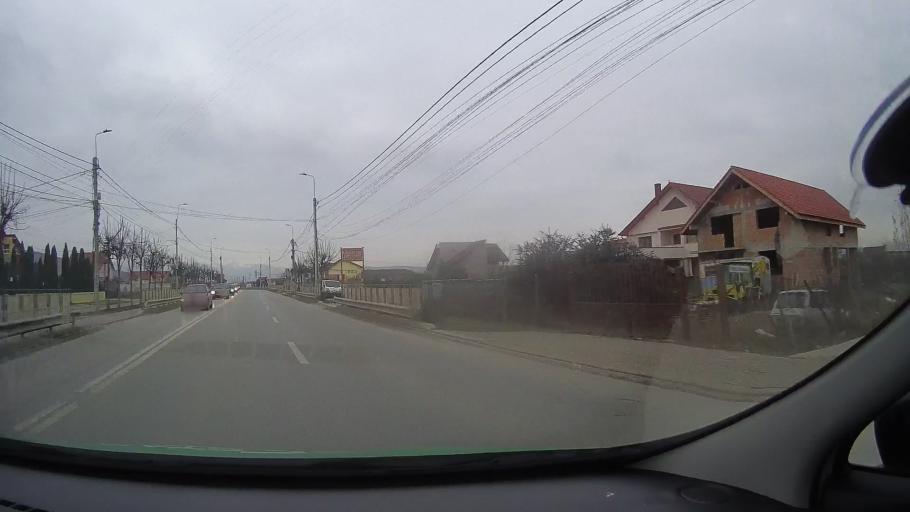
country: RO
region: Alba
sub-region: Municipiul Alba Iulia
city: Micesti
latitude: 46.0912
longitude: 23.5554
